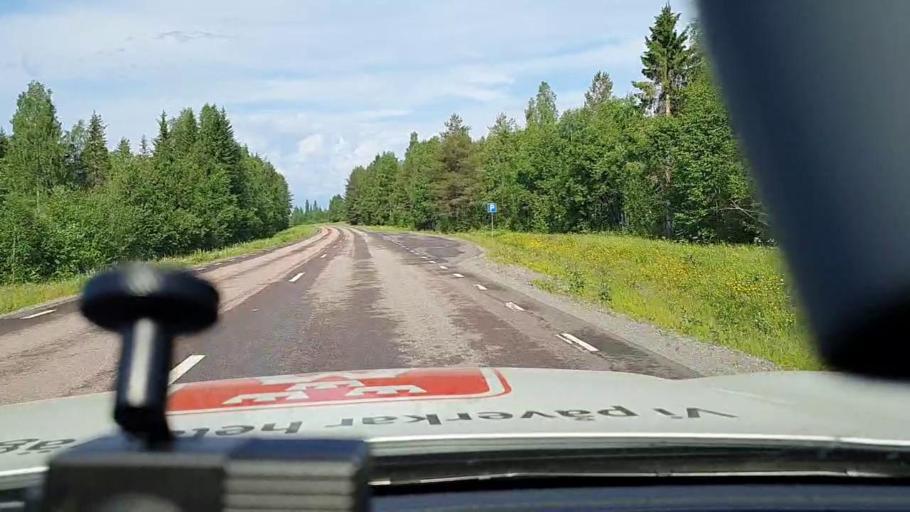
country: SE
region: Norrbotten
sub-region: Alvsbyns Kommun
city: AElvsbyn
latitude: 66.0215
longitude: 21.1331
